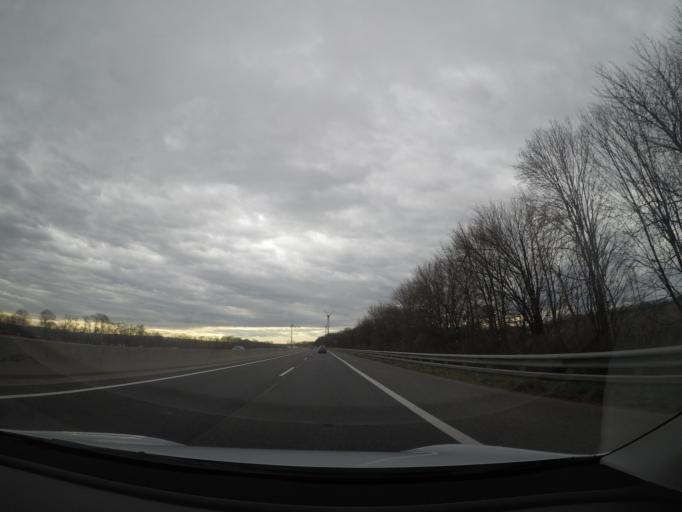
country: AT
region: Lower Austria
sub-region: Politischer Bezirk Baden
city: Ebreichsdorf
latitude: 47.9525
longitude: 16.3675
